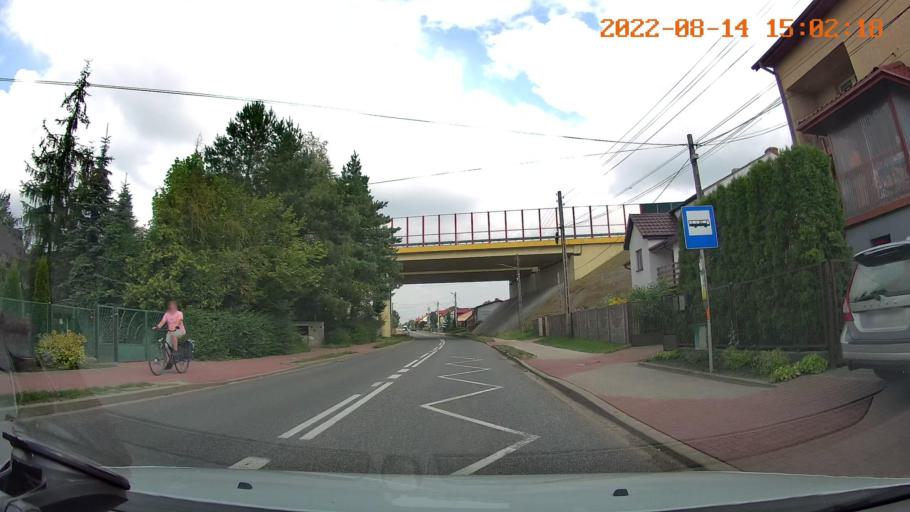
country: PL
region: Swietokrzyskie
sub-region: Powiat kielecki
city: Piekoszow
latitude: 50.8824
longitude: 20.5202
